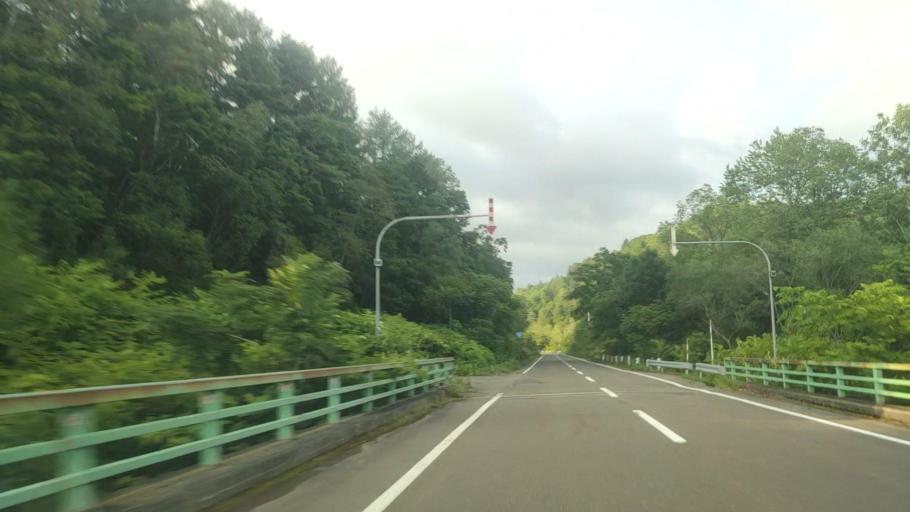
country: JP
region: Hokkaido
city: Bibai
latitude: 43.1356
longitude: 142.0953
